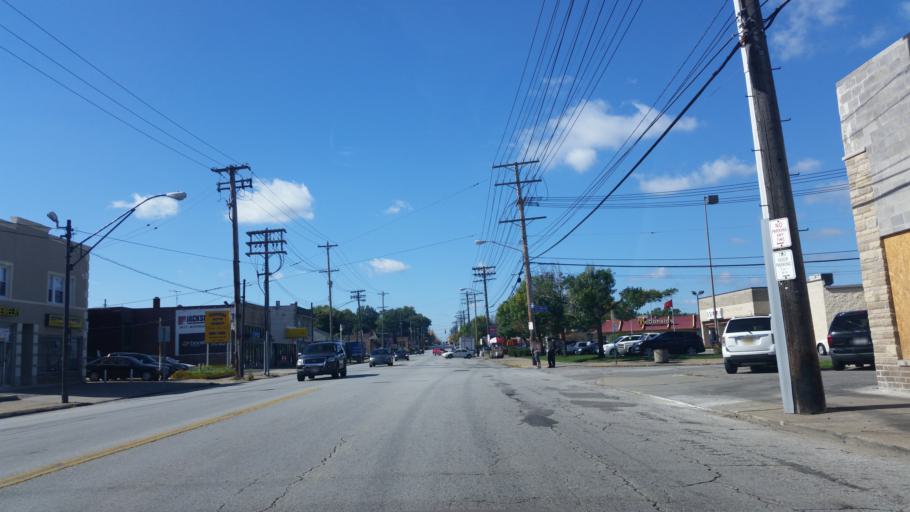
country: US
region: Ohio
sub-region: Cuyahoga County
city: Brooklyn
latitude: 41.4651
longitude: -81.7593
